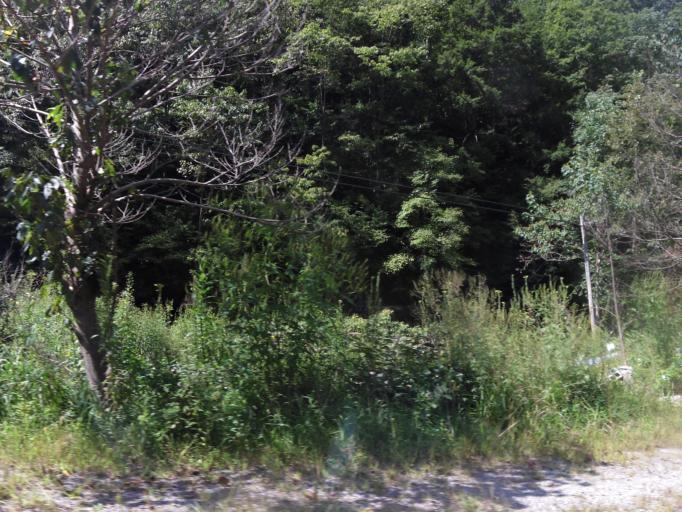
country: US
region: Kentucky
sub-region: Harlan County
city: Loyall
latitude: 36.9634
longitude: -83.3942
